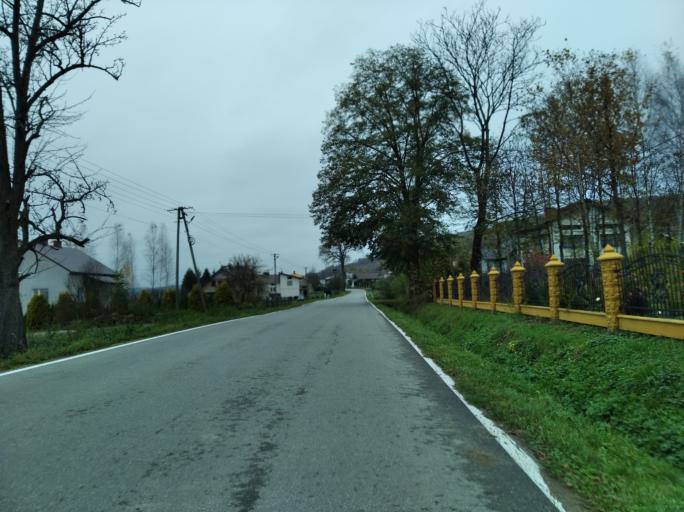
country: PL
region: Subcarpathian Voivodeship
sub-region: Powiat krosnienski
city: Leki
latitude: 49.8222
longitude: 21.6445
